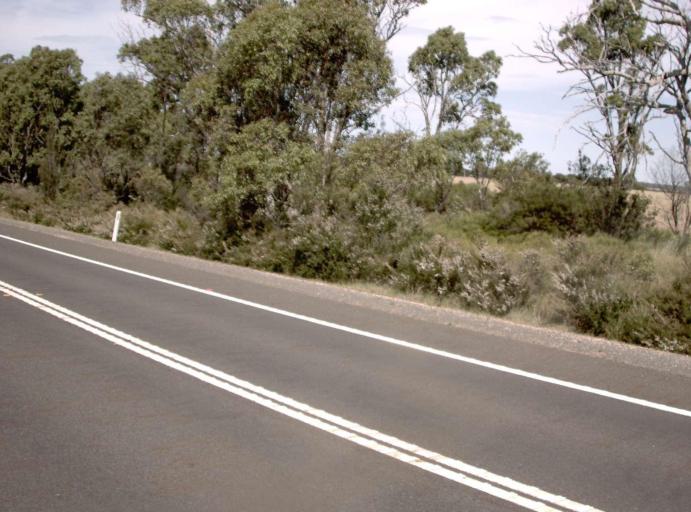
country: AU
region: Victoria
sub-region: East Gippsland
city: Bairnsdale
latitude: -37.8846
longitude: 147.4058
